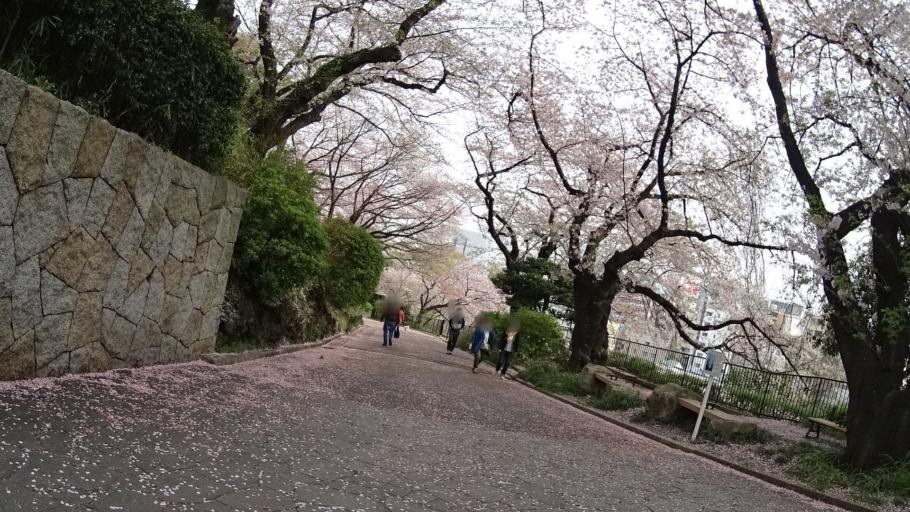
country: JP
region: Kanagawa
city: Yokohama
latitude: 35.4532
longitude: 139.6262
